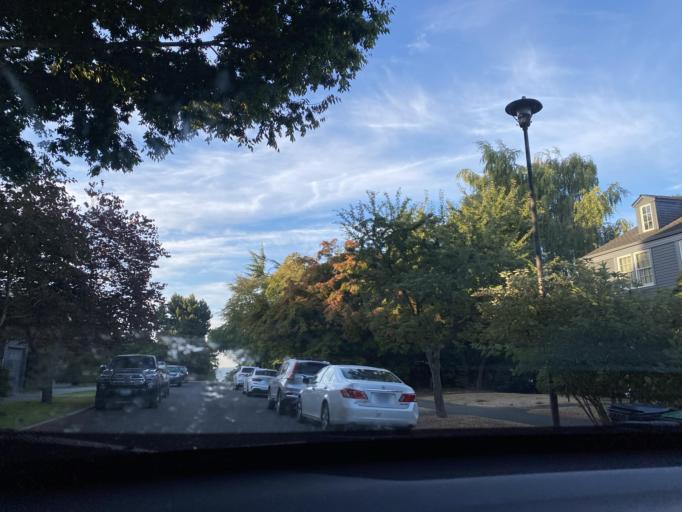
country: US
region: Washington
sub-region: King County
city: Seattle
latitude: 47.6331
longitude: -122.3664
